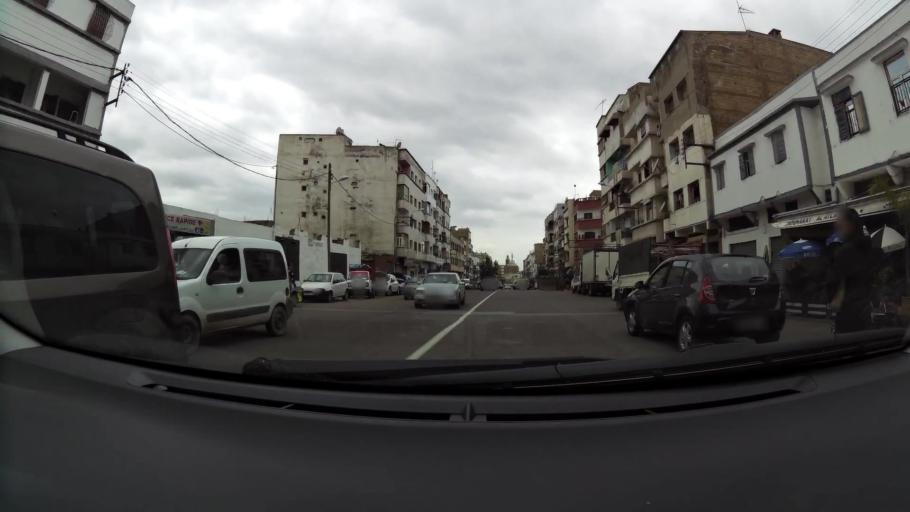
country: MA
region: Grand Casablanca
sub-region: Casablanca
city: Casablanca
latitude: 33.5818
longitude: -7.5543
